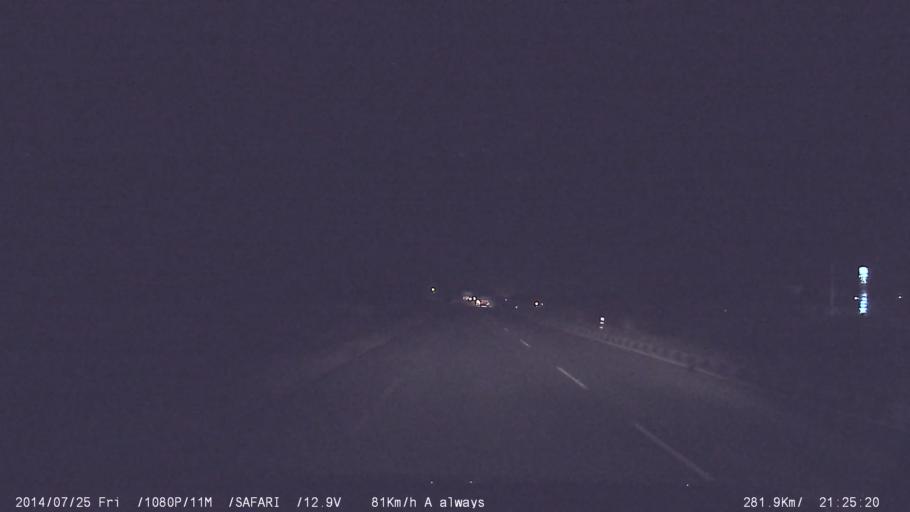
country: IN
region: Tamil Nadu
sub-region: Erode
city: Vijayapuri
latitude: 11.2524
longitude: 77.5411
